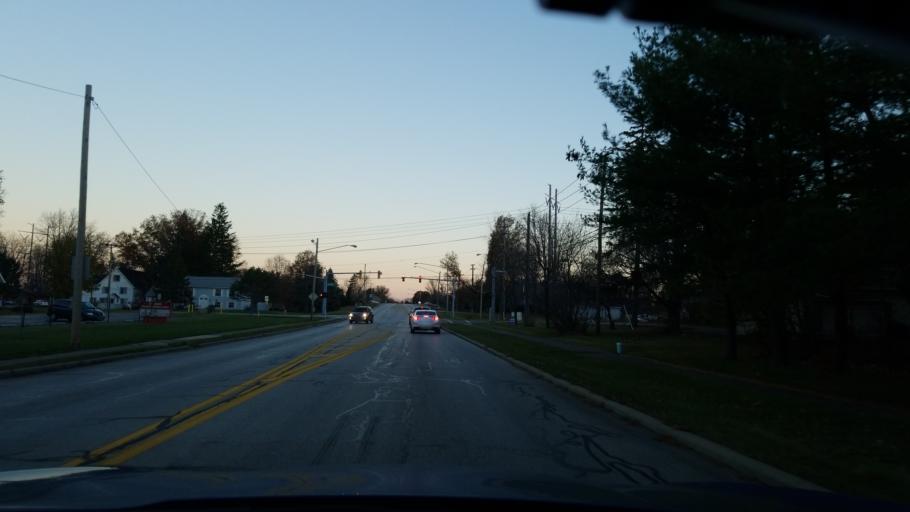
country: US
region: Ohio
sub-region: Cuyahoga County
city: Berea
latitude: 41.3445
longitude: -81.8575
